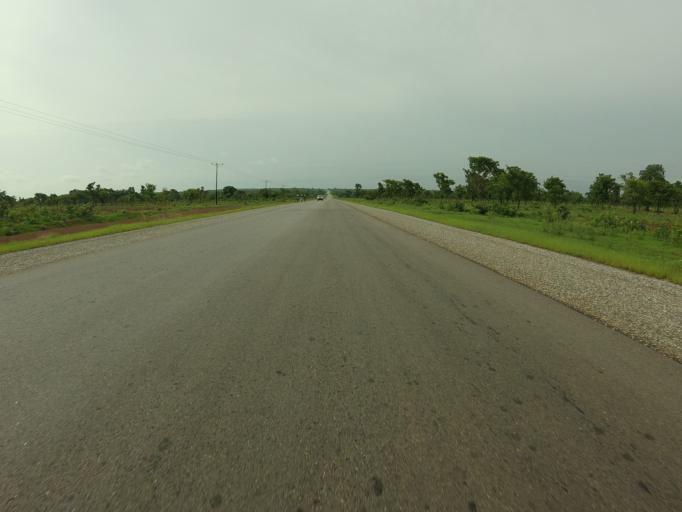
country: GH
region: Northern
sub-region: Yendi
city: Yendi
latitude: 9.6340
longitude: -0.0607
